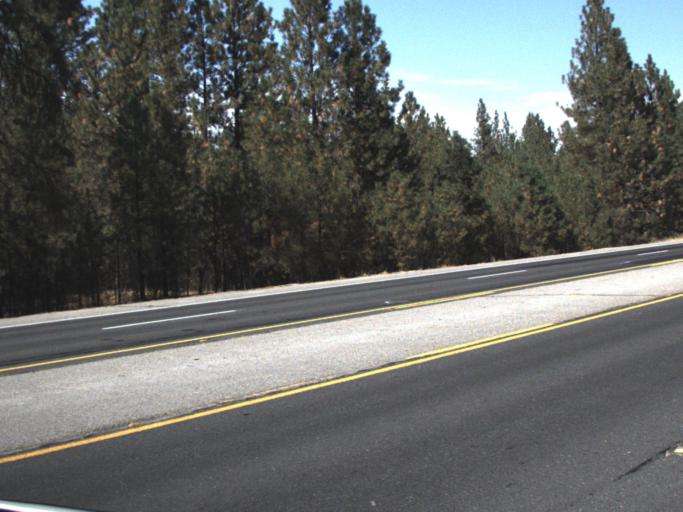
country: US
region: Washington
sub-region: Spokane County
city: Country Homes
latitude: 47.7641
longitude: -117.3883
